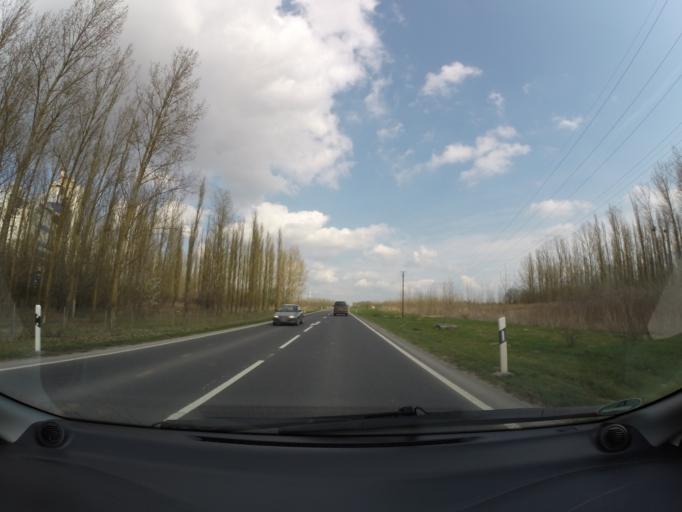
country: DE
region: Brandenburg
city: Petershagen
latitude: 52.4856
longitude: 13.8381
